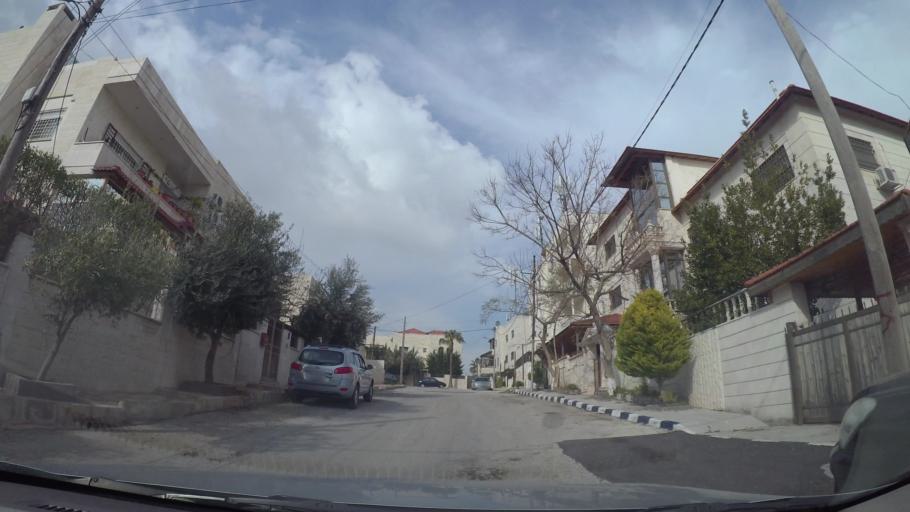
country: JO
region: Amman
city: Umm as Summaq
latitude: 31.8863
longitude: 35.8697
